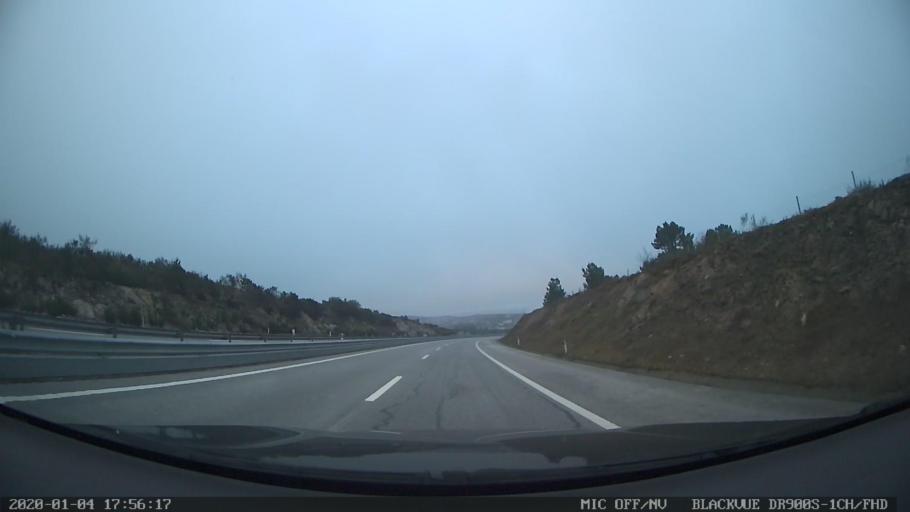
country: PT
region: Vila Real
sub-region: Vila Pouca de Aguiar
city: Vila Pouca de Aguiar
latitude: 41.5026
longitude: -7.7100
